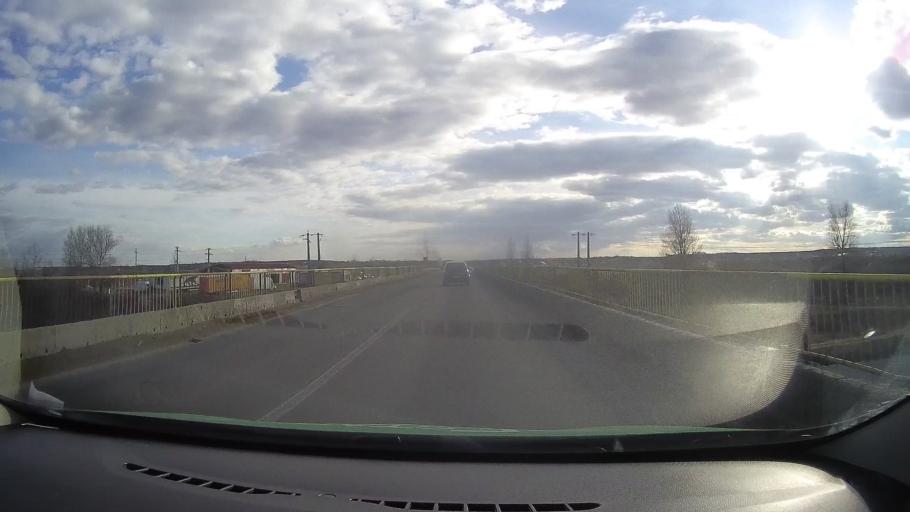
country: RO
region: Dambovita
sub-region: Comuna Lucieni
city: Lucieni
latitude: 44.8590
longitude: 25.4183
